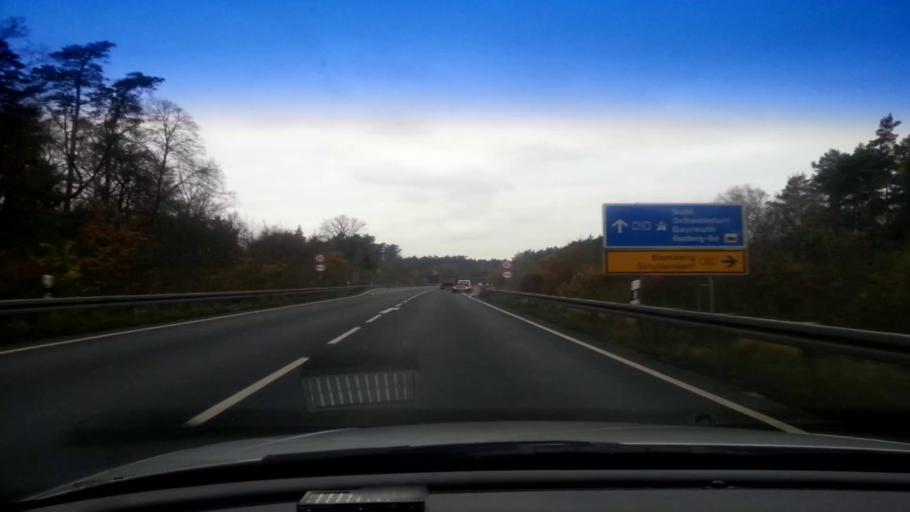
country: DE
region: Bavaria
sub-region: Upper Franconia
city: Strullendorf
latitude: 49.8630
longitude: 10.9493
